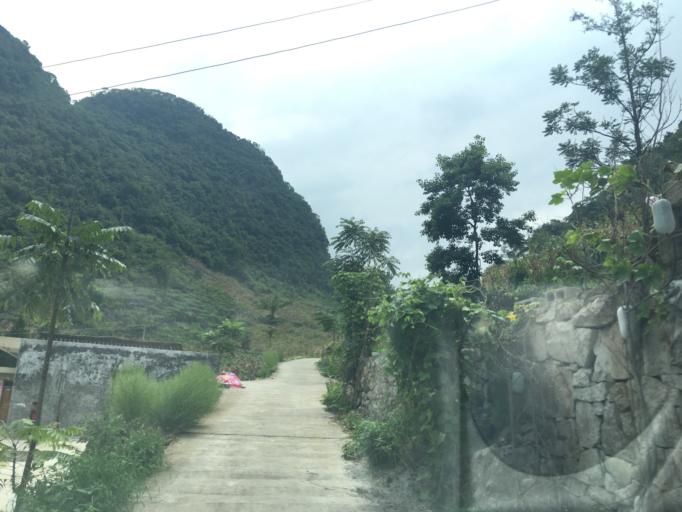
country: CN
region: Guangxi Zhuangzu Zizhiqu
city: Xinzhou
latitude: 25.2332
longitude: 105.6489
